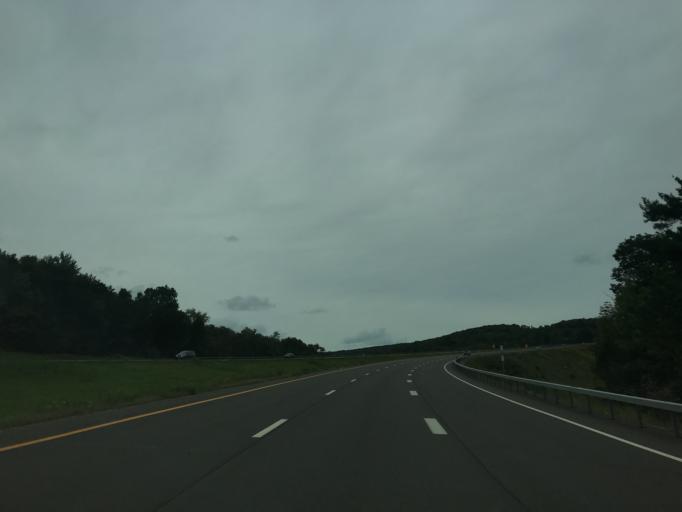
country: US
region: New York
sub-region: Broome County
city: Chenango Bridge
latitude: 42.1773
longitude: -75.7505
